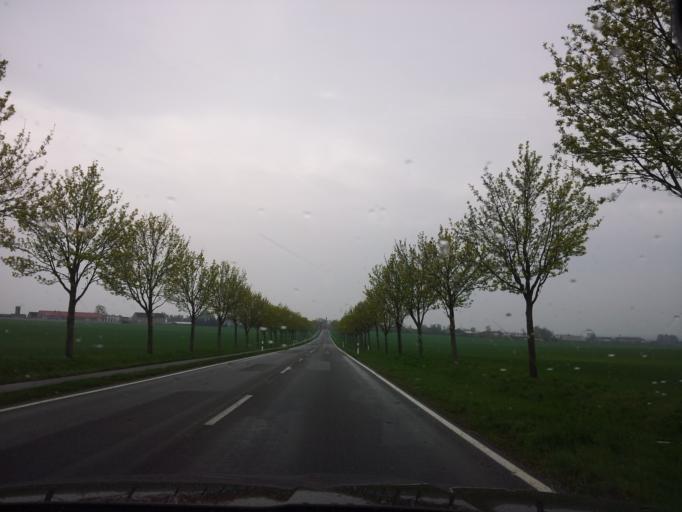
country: DE
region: Saxony-Anhalt
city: Kropstadt
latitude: 52.0102
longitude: 12.7862
